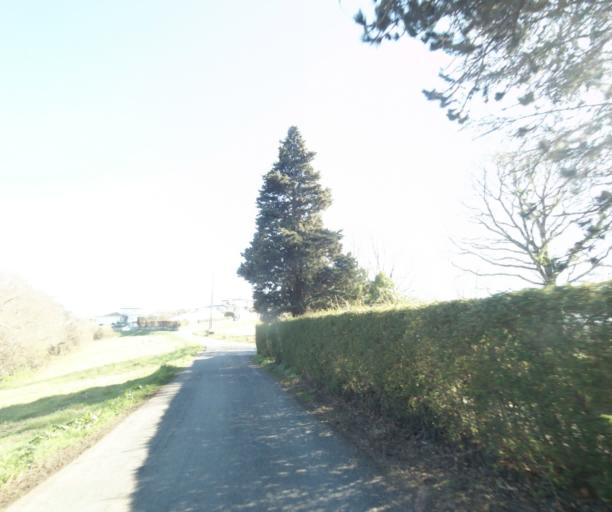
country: FR
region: Aquitaine
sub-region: Departement des Pyrenees-Atlantiques
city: Urrugne
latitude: 43.3665
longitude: -1.7353
